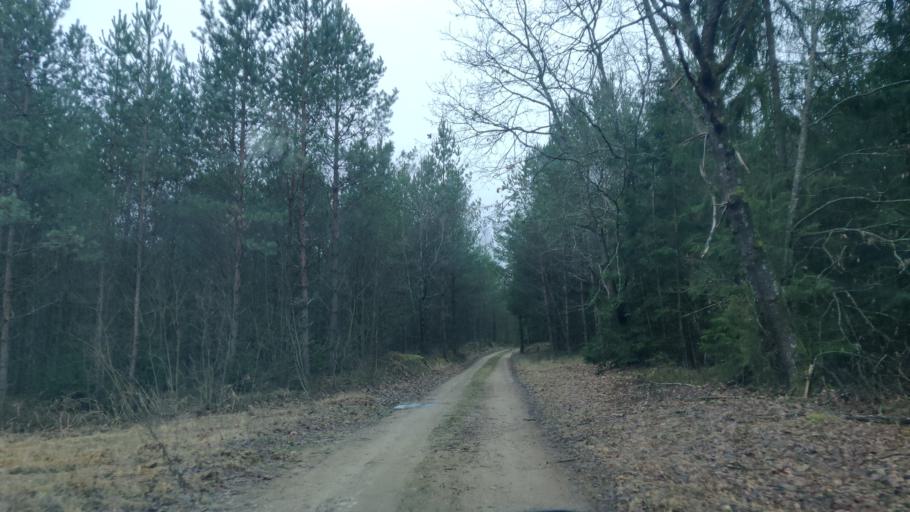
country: LT
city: Trakai
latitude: 54.5630
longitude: 24.9618
